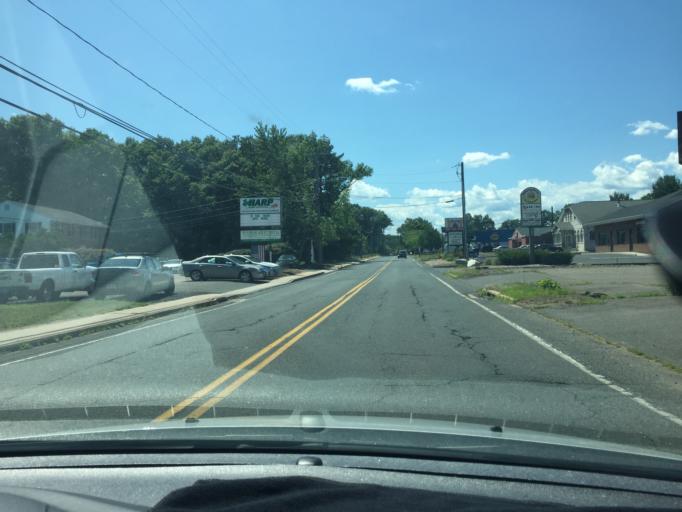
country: US
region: Connecticut
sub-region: Hartford County
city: Windsor Locks
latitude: 41.9320
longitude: -72.6606
